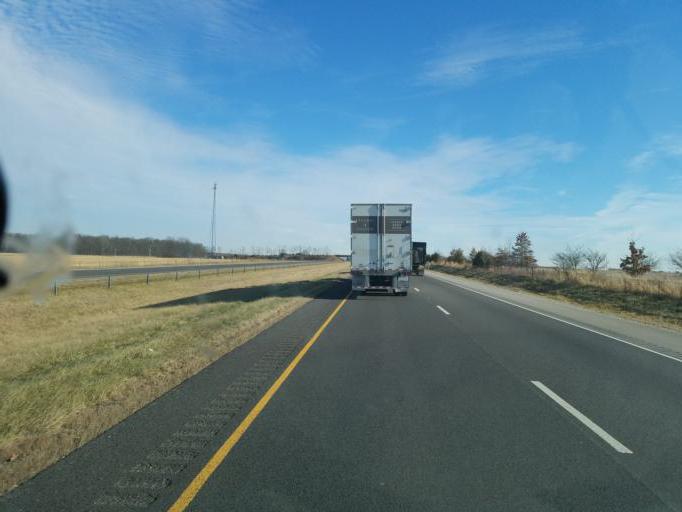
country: US
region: Indiana
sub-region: Wayne County
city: Centerville
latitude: 39.8571
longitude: -85.0486
